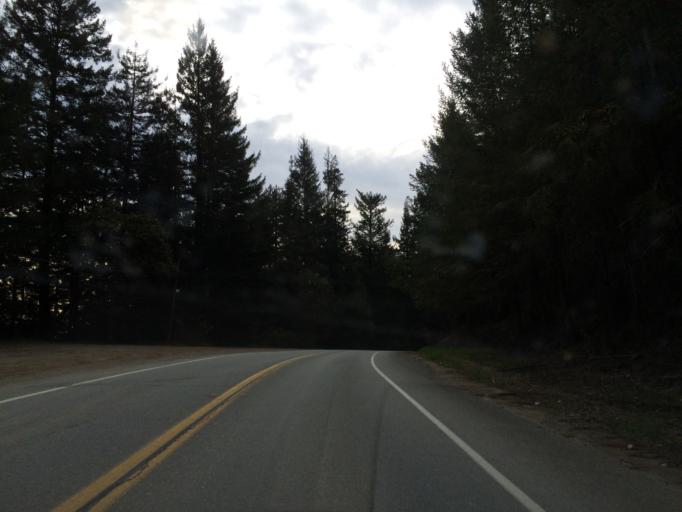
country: US
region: California
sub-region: Santa Cruz County
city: Felton
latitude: 37.0303
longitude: -122.1022
